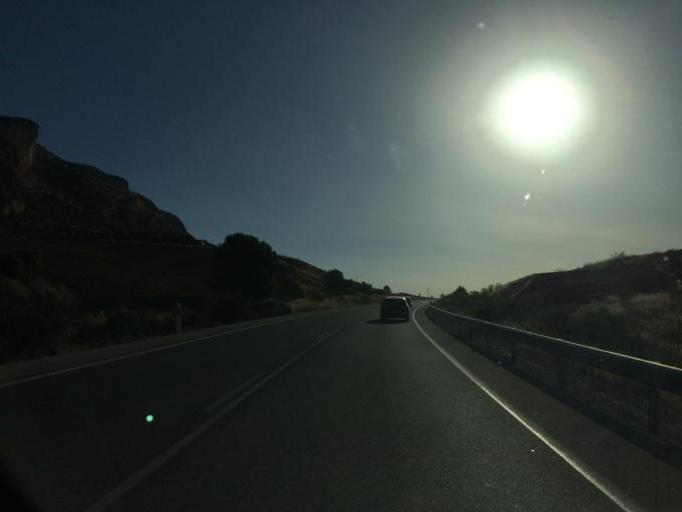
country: ES
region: Andalusia
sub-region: Provincia de Malaga
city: Teba
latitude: 36.9627
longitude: -4.8552
